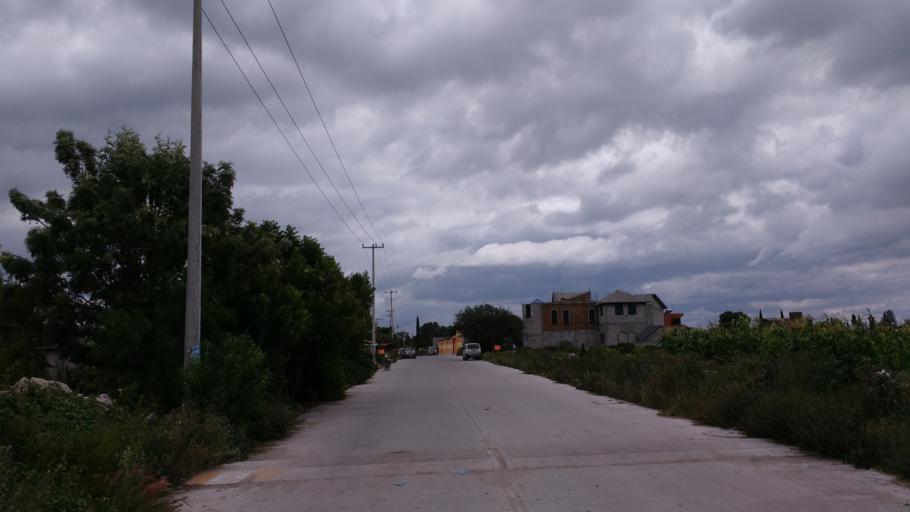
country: MX
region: Hidalgo
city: Mixquiahuala de Juarez
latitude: 20.2333
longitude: -99.2483
